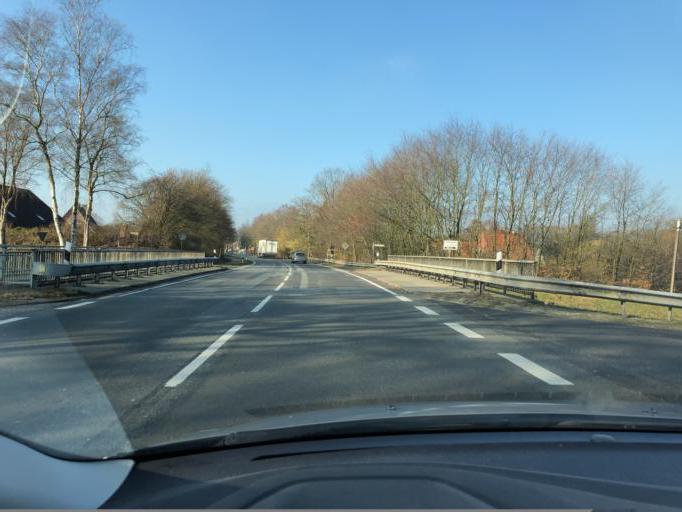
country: DE
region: Lower Saxony
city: Schwerinsdorf
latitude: 53.3069
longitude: 7.7669
